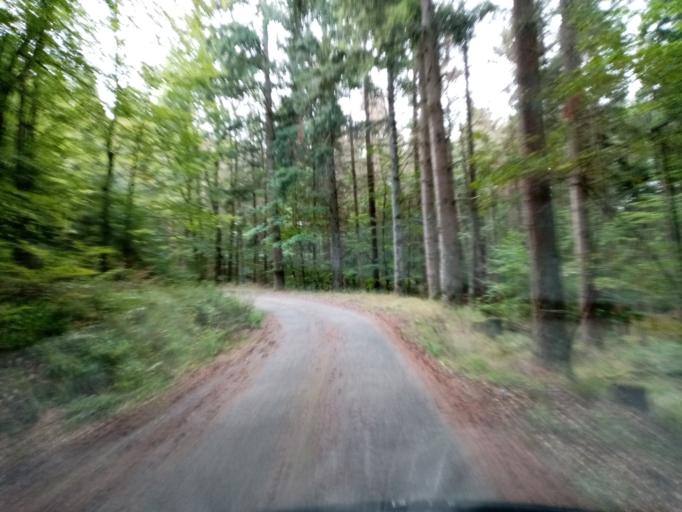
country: FR
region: Alsace
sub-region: Departement du Bas-Rhin
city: Dambach-la-Ville
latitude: 48.3306
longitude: 7.3926
